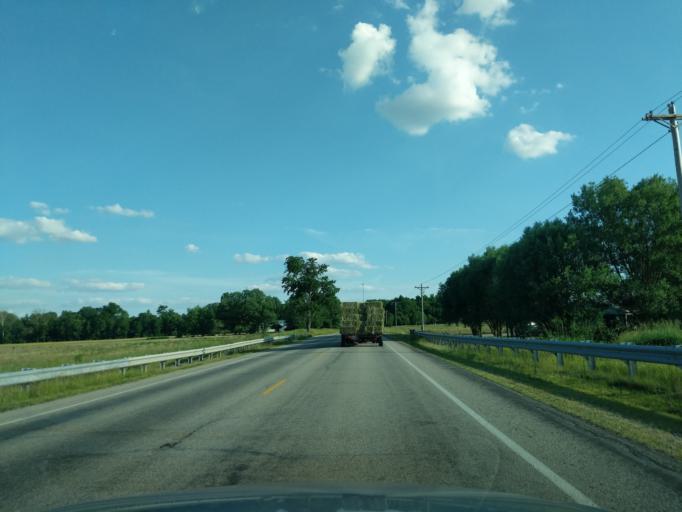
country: US
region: Indiana
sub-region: Huntington County
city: Roanoke
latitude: 41.0124
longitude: -85.4707
